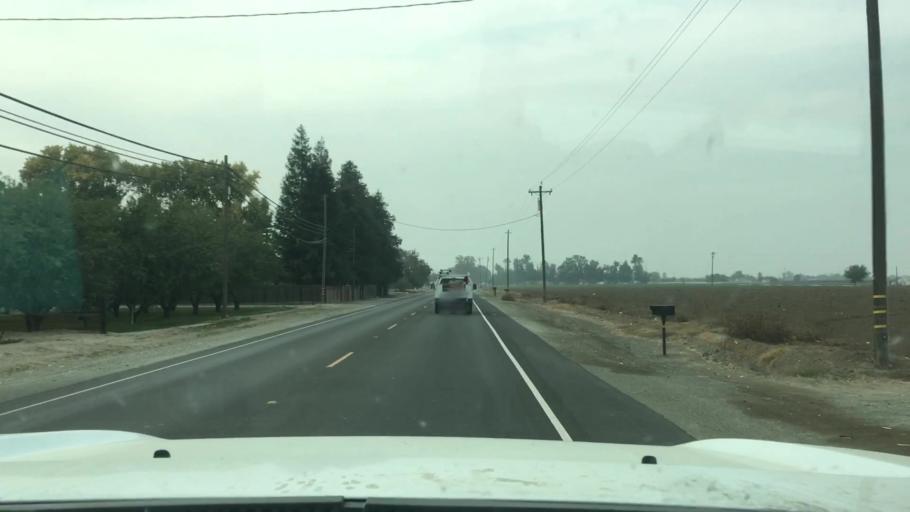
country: US
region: California
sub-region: San Joaquin County
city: French Camp
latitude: 37.8684
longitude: -121.2435
